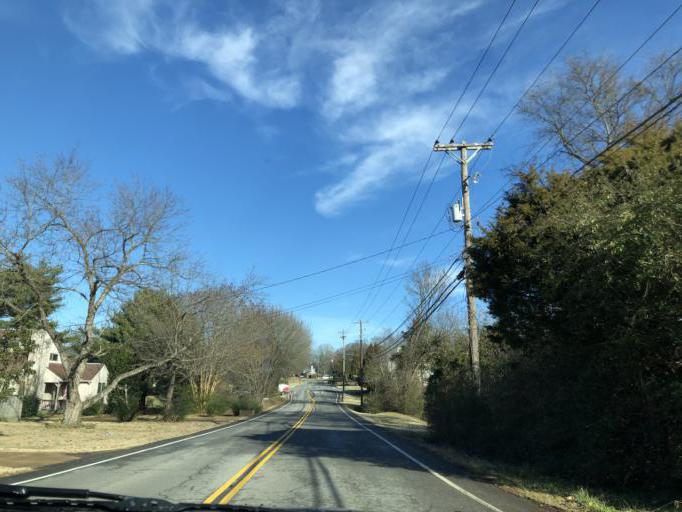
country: US
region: Tennessee
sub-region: Wilson County
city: Green Hill
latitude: 36.1628
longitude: -86.5850
